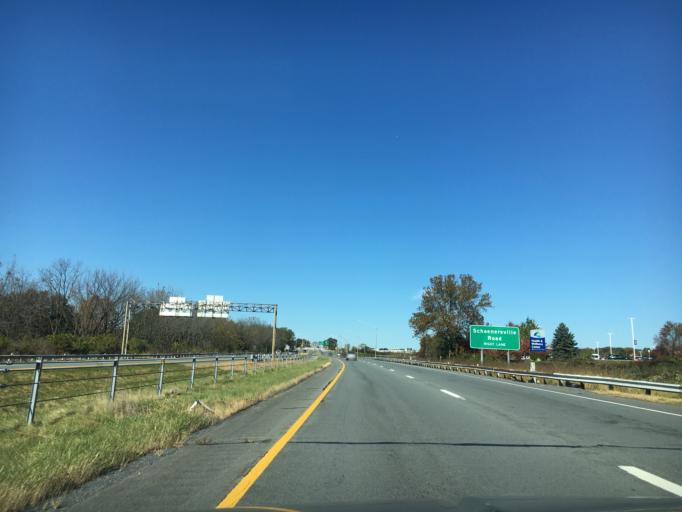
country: US
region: Pennsylvania
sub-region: Northampton County
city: Bethlehem
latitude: 40.6426
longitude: -75.4108
